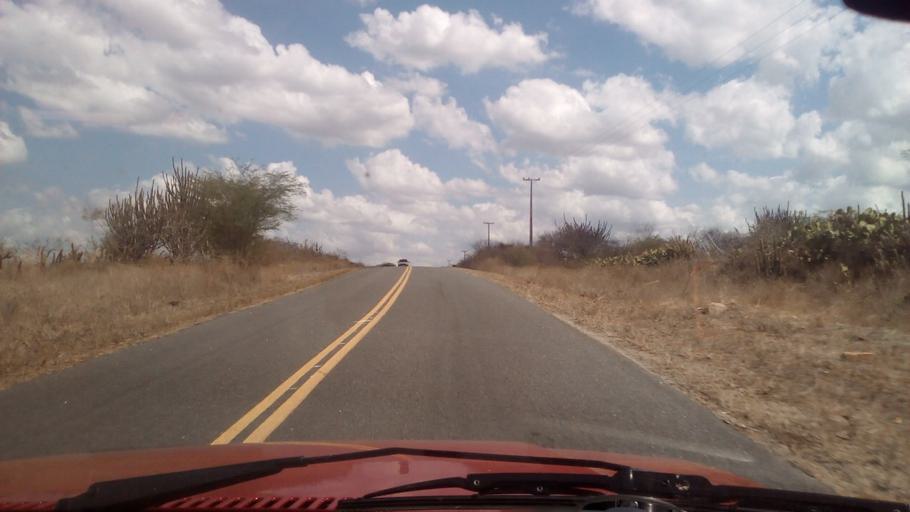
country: BR
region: Paraiba
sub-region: Cacimba De Dentro
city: Cacimba de Dentro
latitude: -6.6966
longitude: -35.7373
